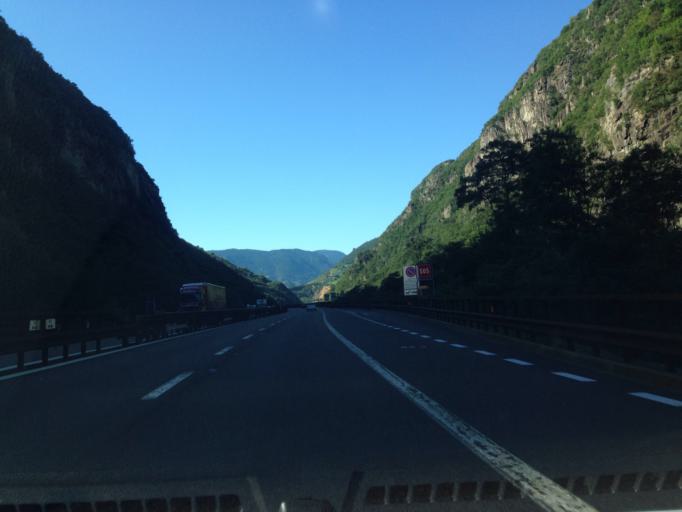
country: IT
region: Trentino-Alto Adige
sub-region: Bolzano
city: Fie Allo Sciliar
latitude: 46.5486
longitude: 11.5121
